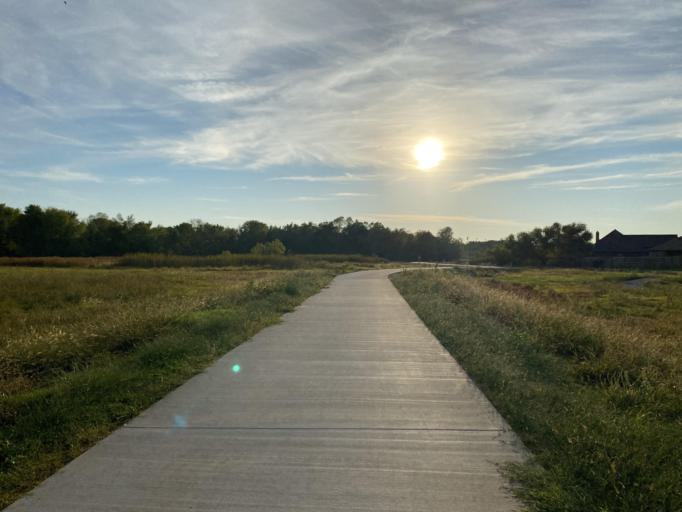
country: US
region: Arkansas
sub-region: Washington County
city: Johnson
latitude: 36.1044
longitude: -94.1995
